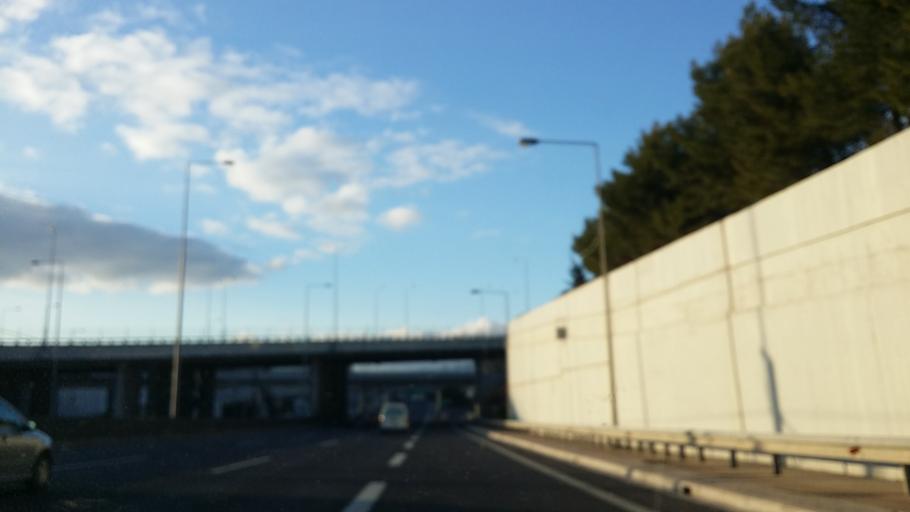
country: GR
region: Attica
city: Pefki
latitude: 38.0499
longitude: 23.7843
